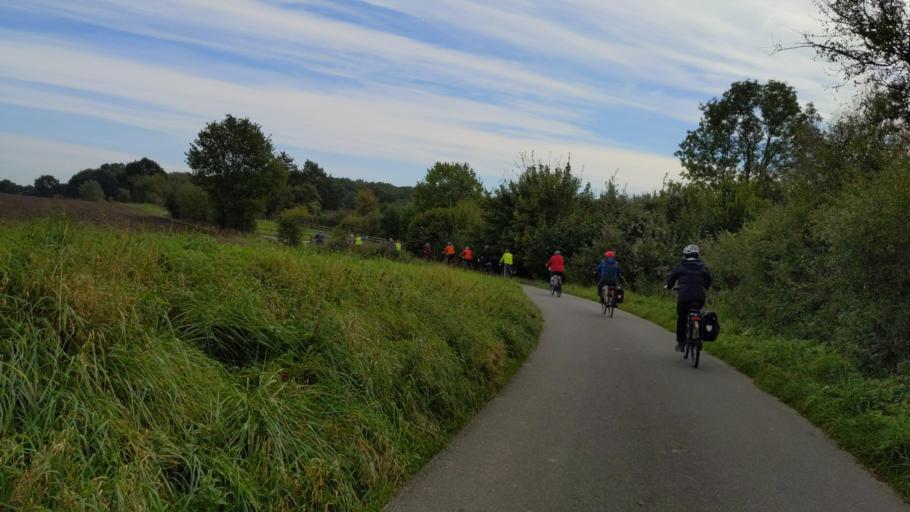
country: DE
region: Schleswig-Holstein
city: Rehhorst
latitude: 53.8690
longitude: 10.4778
